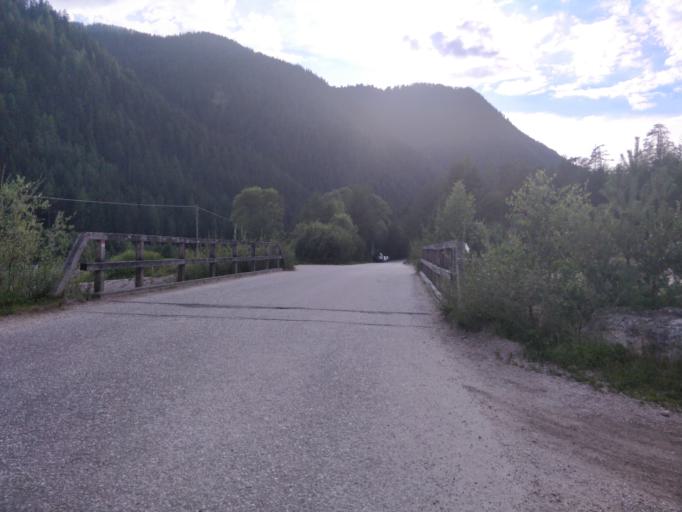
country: IT
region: Trentino-Alto Adige
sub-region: Bolzano
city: San Vigilio
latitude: 46.6885
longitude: 11.9493
